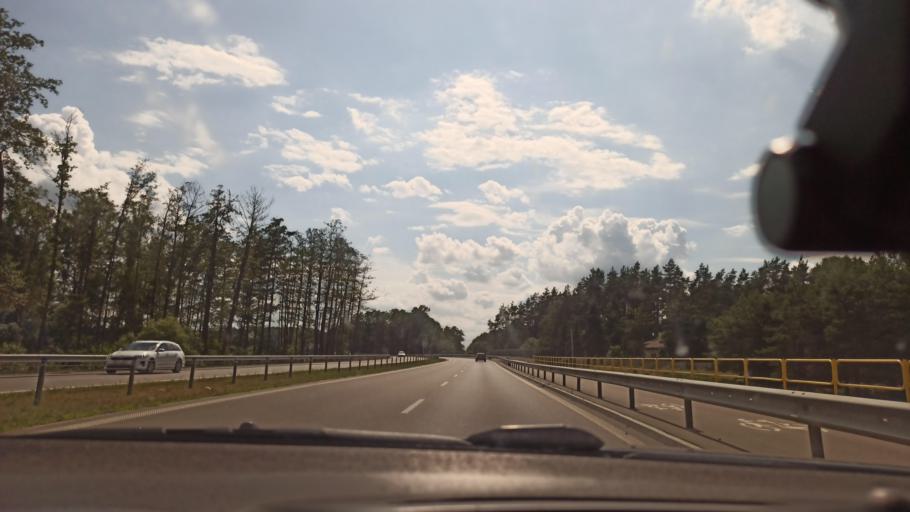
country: PL
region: Podlasie
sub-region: Powiat bialostocki
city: Turosn Koscielna
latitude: 53.0645
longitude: 23.0688
